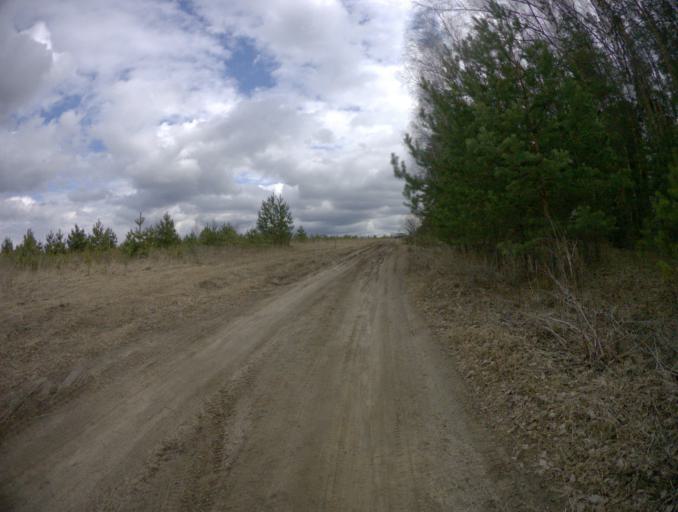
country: RU
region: Vladimir
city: Orgtrud
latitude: 56.0650
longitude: 40.6873
